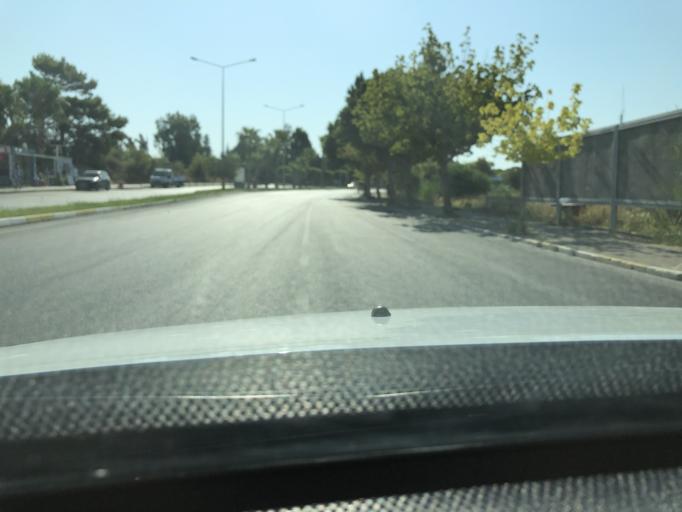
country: TR
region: Antalya
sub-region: Manavgat
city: Side
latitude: 36.7815
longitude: 31.3920
